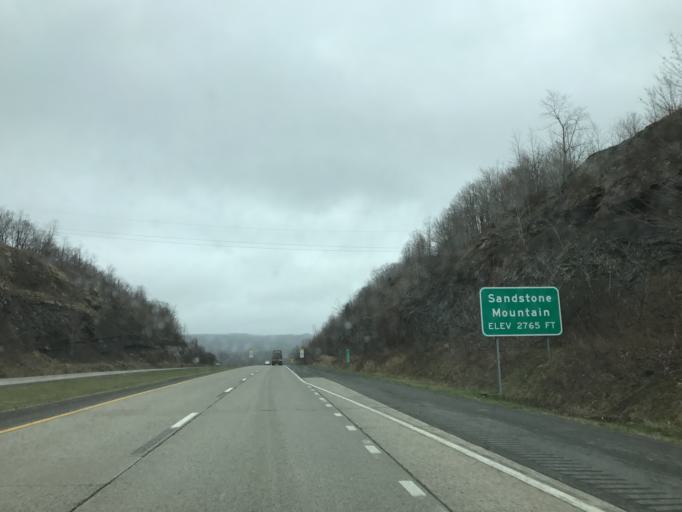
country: US
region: West Virginia
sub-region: Raleigh County
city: Shady Spring
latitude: 37.7705
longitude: -80.9834
